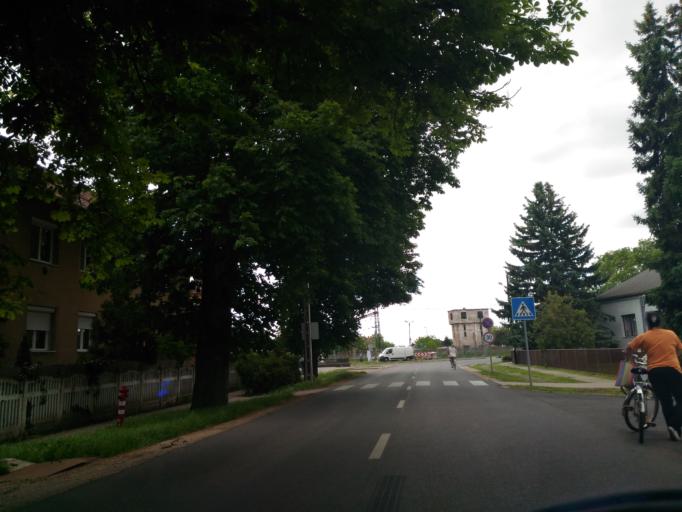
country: HU
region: Fejer
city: Pusztaszabolcs
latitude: 47.1389
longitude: 18.7594
